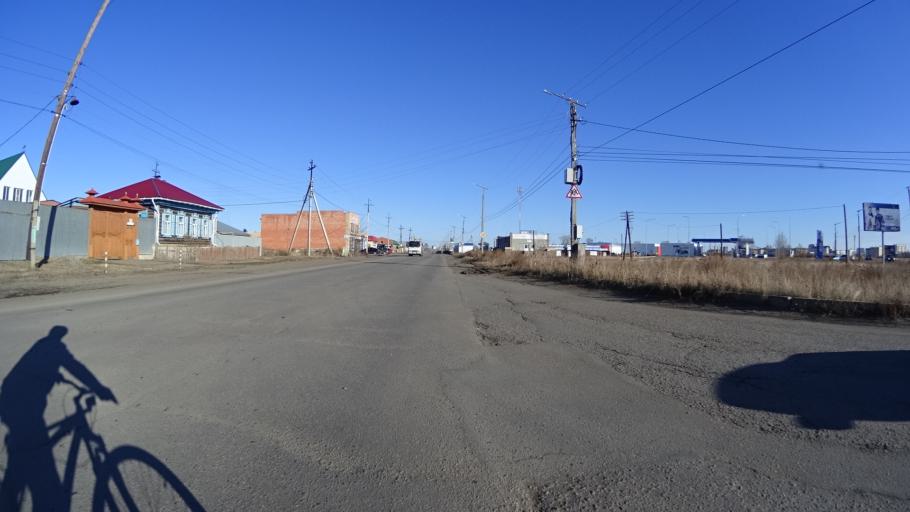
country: RU
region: Chelyabinsk
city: Troitsk
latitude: 54.0828
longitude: 61.5169
